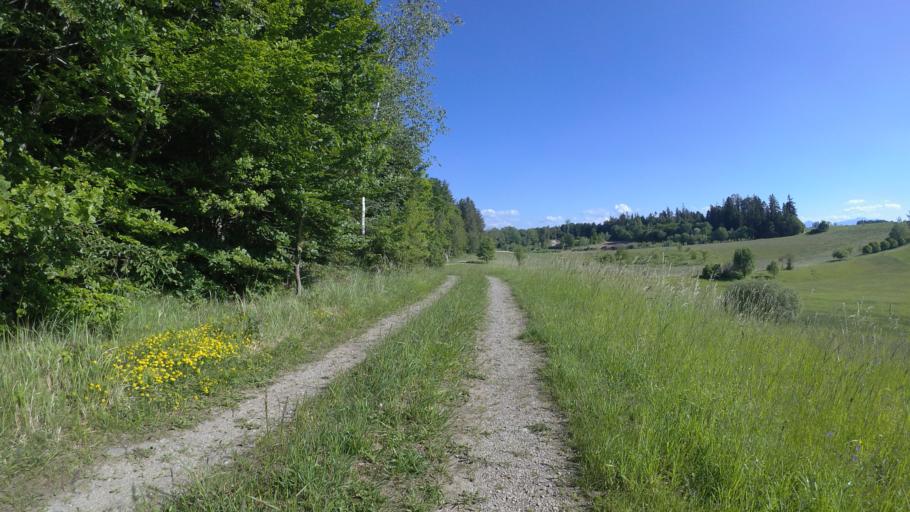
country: DE
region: Bavaria
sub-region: Upper Bavaria
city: Traunreut
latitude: 47.9462
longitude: 12.5539
